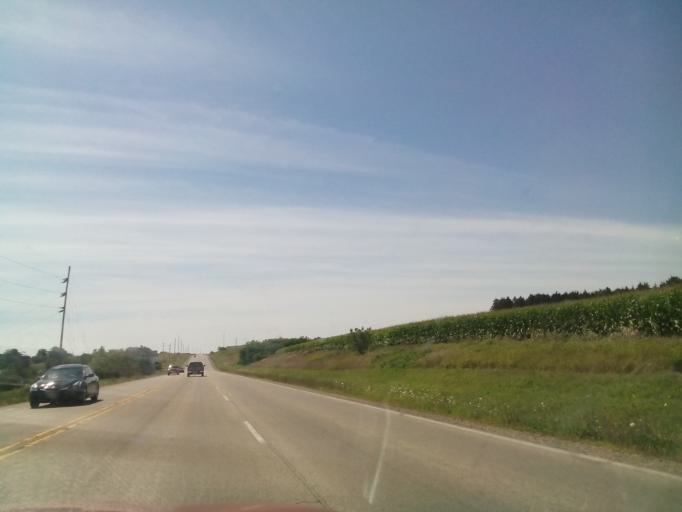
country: US
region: Wisconsin
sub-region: Green County
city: Monticello
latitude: 42.6862
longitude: -89.6169
